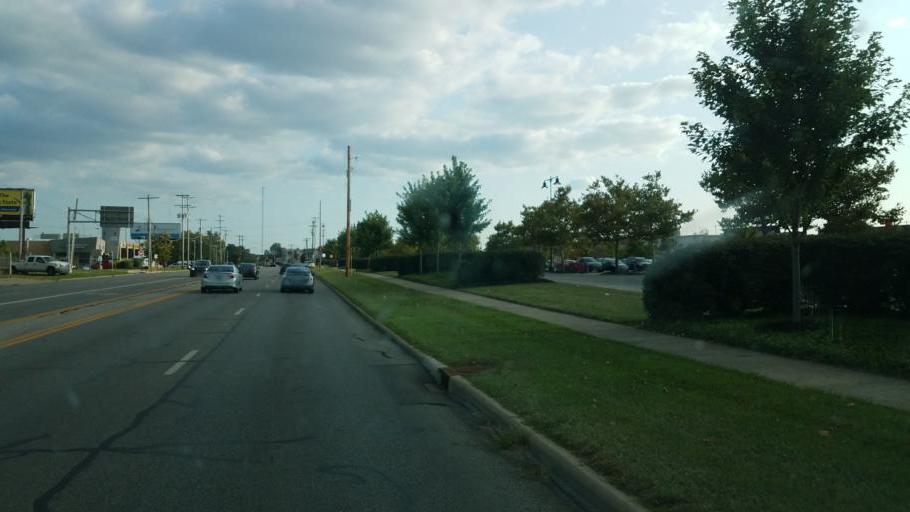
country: US
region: Ohio
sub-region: Franklin County
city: Grandview Heights
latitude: 39.9942
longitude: -83.0256
